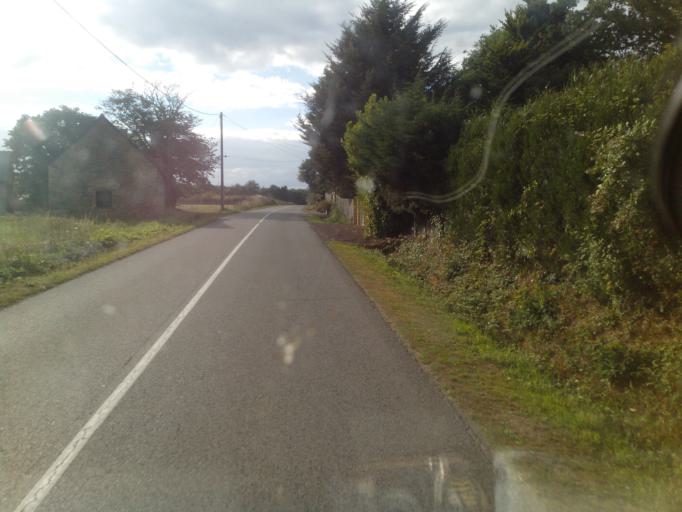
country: FR
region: Brittany
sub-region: Departement d'Ille-et-Vilaine
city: Plelan-le-Grand
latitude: 48.0043
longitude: -2.1169
